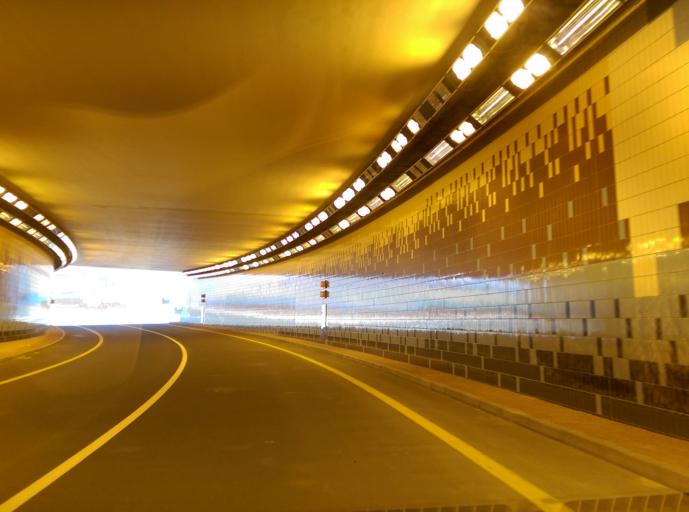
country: AE
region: Dubai
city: Dubai
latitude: 25.0846
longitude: 55.1976
